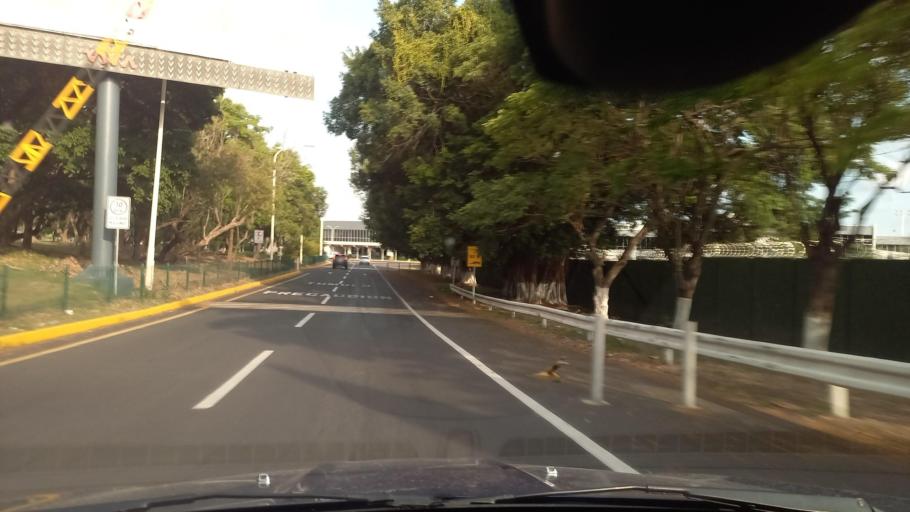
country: SV
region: La Paz
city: El Rosario
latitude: 13.4456
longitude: -89.0598
